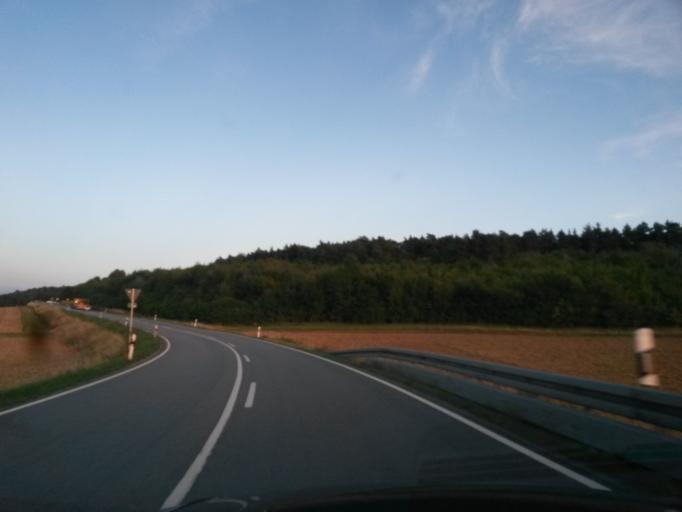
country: DE
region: Bavaria
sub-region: Regierungsbezirk Unterfranken
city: Marktheidenfeld
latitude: 49.8143
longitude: 9.6370
